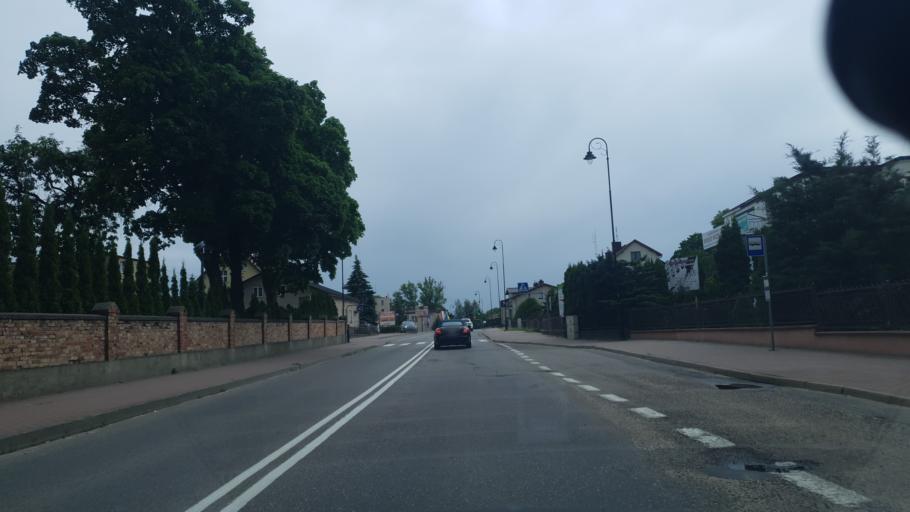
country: PL
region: Pomeranian Voivodeship
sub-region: Powiat kartuski
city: Przodkowo
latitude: 54.3787
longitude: 18.2877
